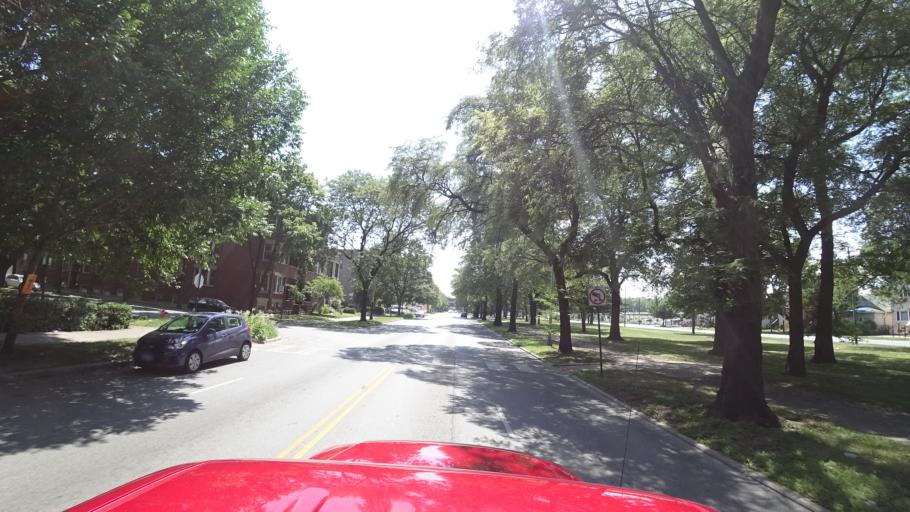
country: US
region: Illinois
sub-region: Cook County
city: Chicago
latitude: 41.8296
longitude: -87.6845
